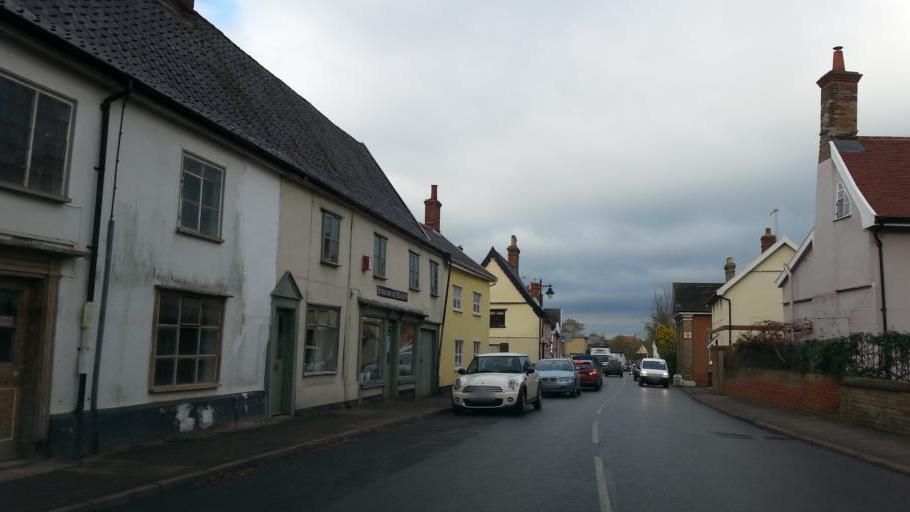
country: GB
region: England
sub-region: Norfolk
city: Harleston
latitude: 52.3184
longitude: 1.2726
